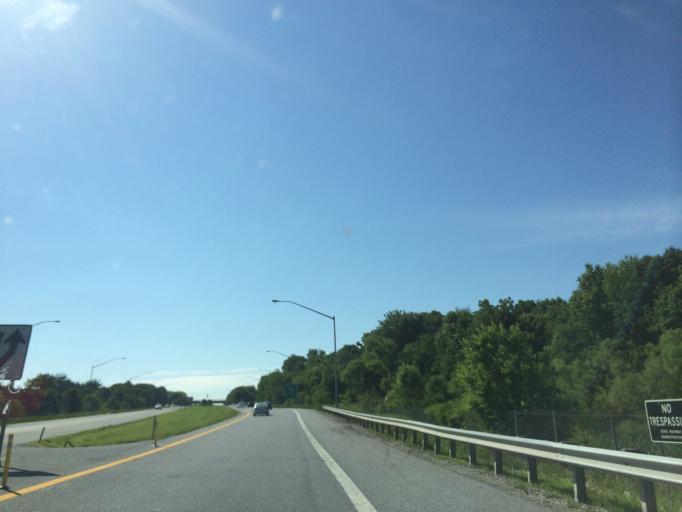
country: US
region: Maryland
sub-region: Howard County
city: Highland
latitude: 39.2114
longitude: -76.9495
